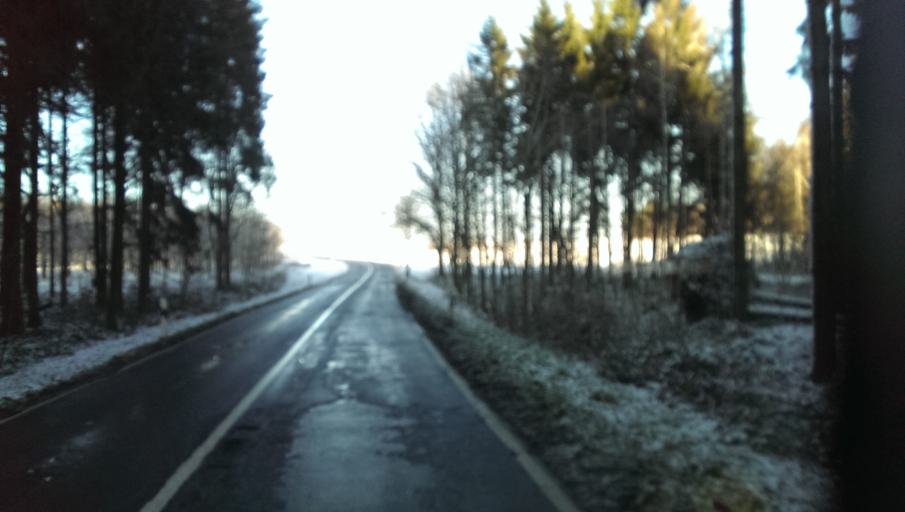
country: DE
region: Saxony
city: Dippoldiswalde
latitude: 50.8991
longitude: 13.6196
